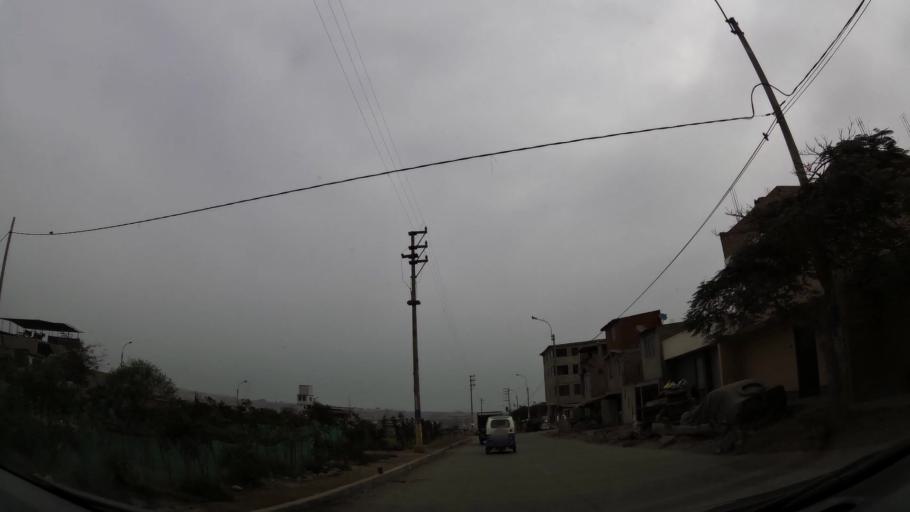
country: PE
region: Lima
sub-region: Lima
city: Surco
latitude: -12.2144
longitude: -76.9507
